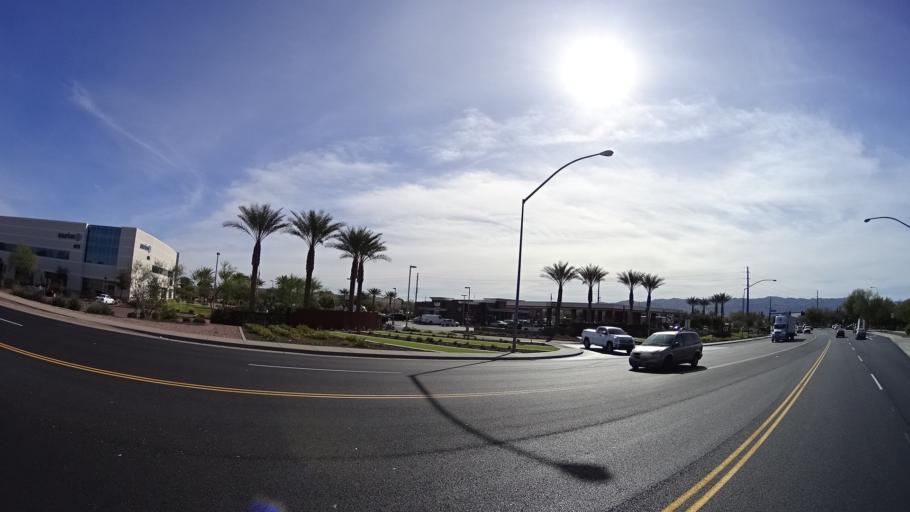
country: US
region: Arizona
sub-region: Maricopa County
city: Guadalupe
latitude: 33.4104
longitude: -112.0117
